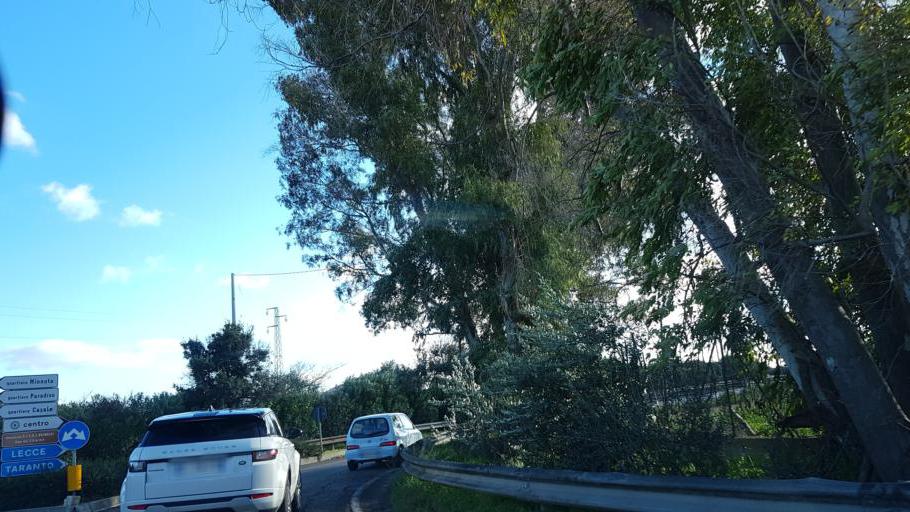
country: IT
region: Apulia
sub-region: Provincia di Brindisi
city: Brindisi
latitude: 40.6348
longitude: 17.9180
